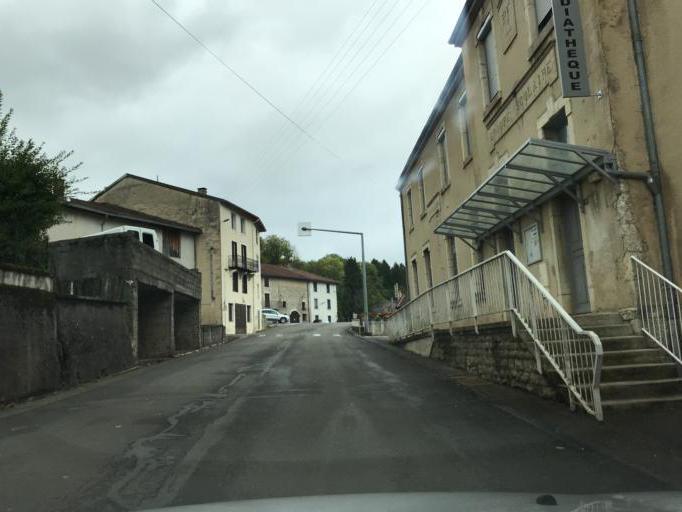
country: FR
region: Rhone-Alpes
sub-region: Departement de l'Ain
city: Coligny
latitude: 46.3937
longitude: 5.4527
